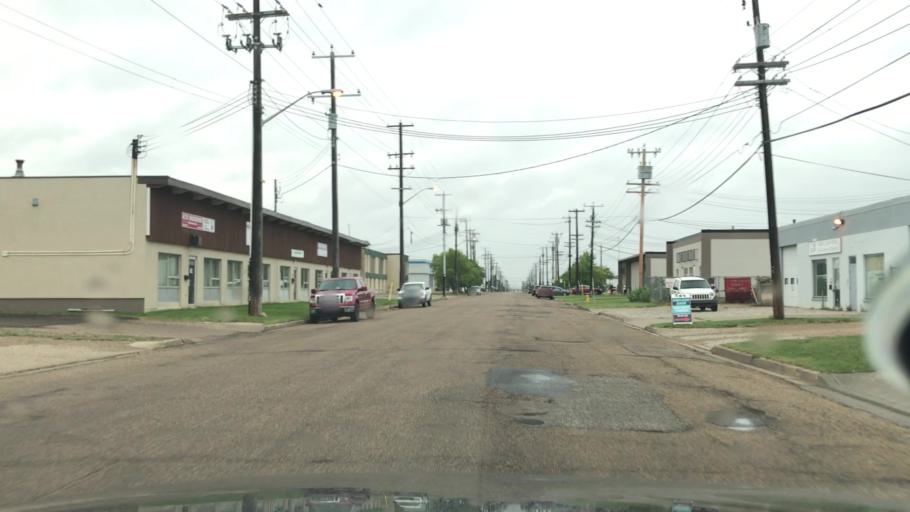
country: CA
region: Alberta
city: Edmonton
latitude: 53.5062
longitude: -113.4446
